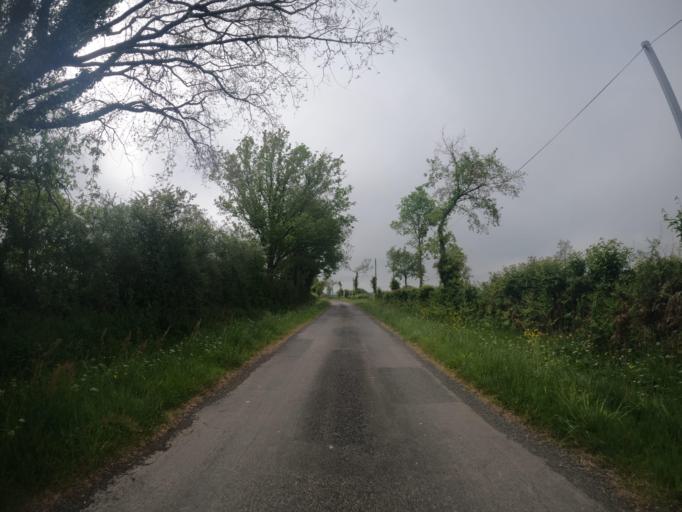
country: FR
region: Poitou-Charentes
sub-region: Departement des Deux-Sevres
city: Chiche
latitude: 46.8380
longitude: -0.3815
